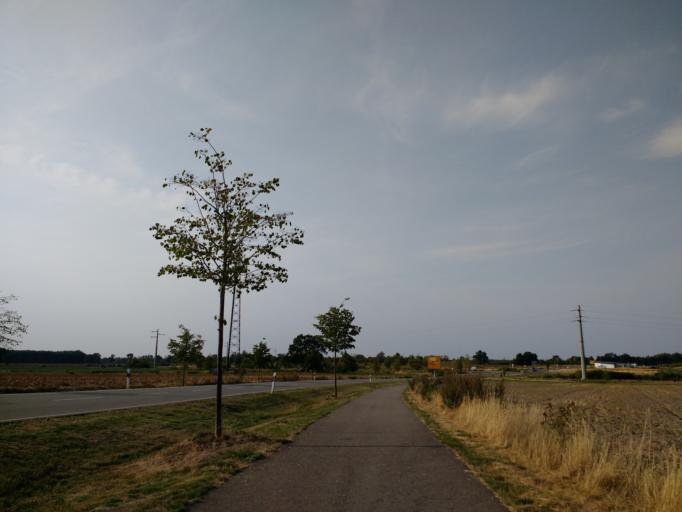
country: DE
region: Lower Saxony
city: Wagenhoff
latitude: 52.5035
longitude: 10.5303
